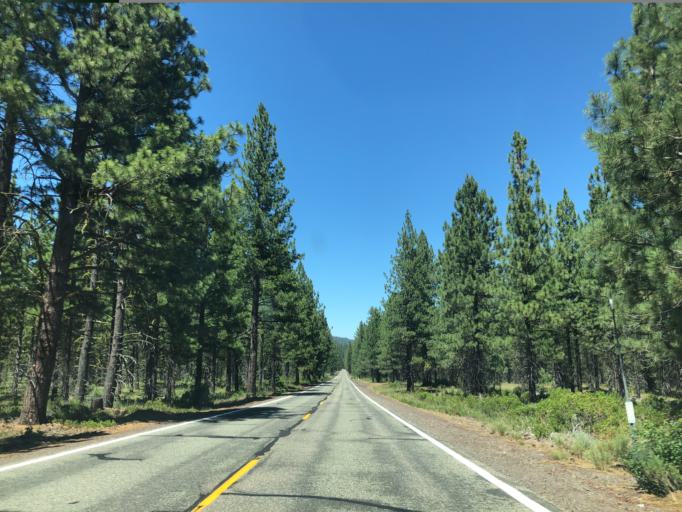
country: US
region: California
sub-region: Shasta County
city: Burney
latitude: 40.6296
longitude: -121.4775
